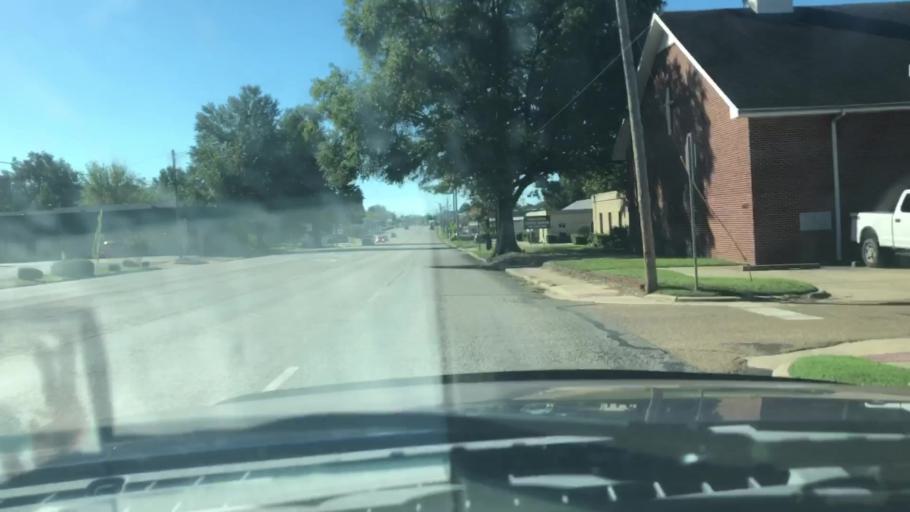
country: US
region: Arkansas
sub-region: Miller County
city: Texarkana
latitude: 33.4424
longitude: -94.0532
